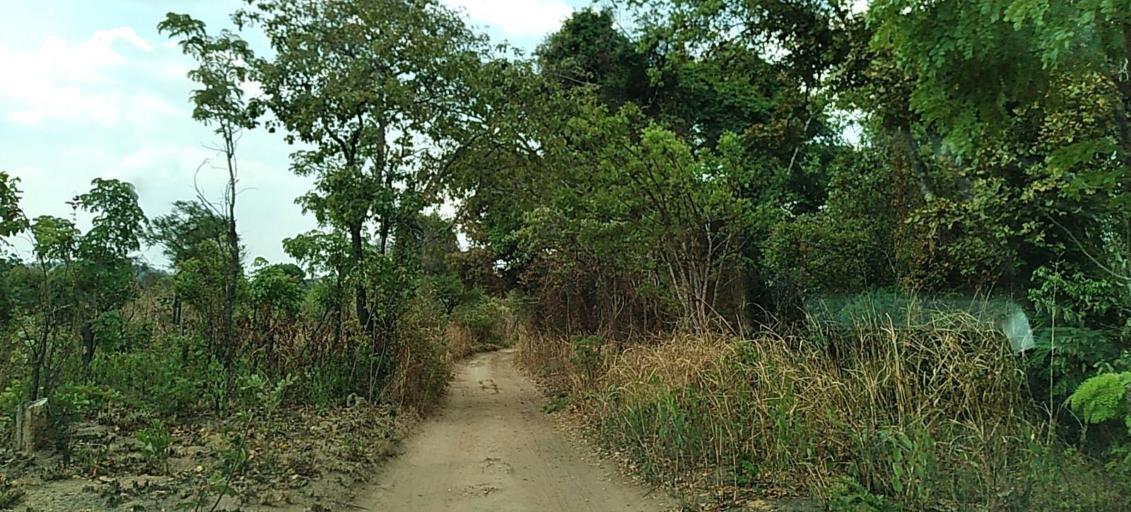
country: ZM
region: Copperbelt
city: Chililabombwe
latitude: -12.3298
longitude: 27.7482
